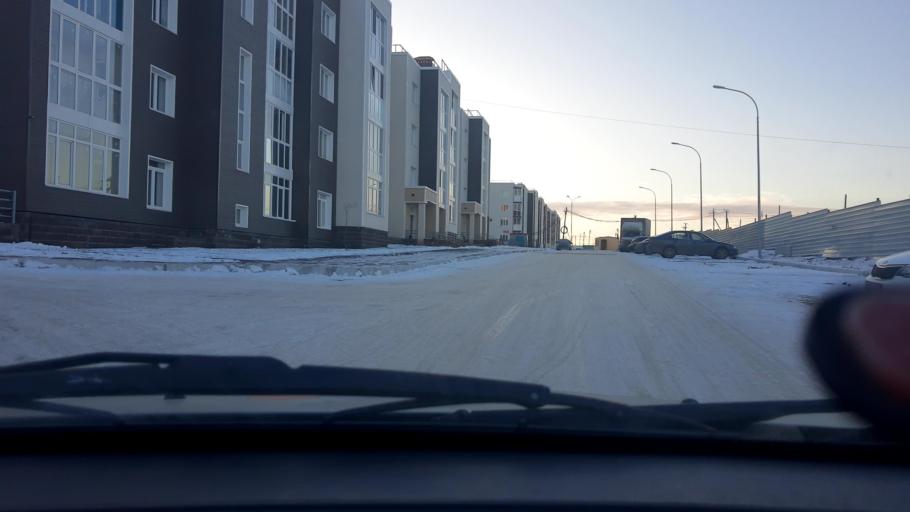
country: RU
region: Bashkortostan
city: Avdon
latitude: 54.7450
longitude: 55.7920
